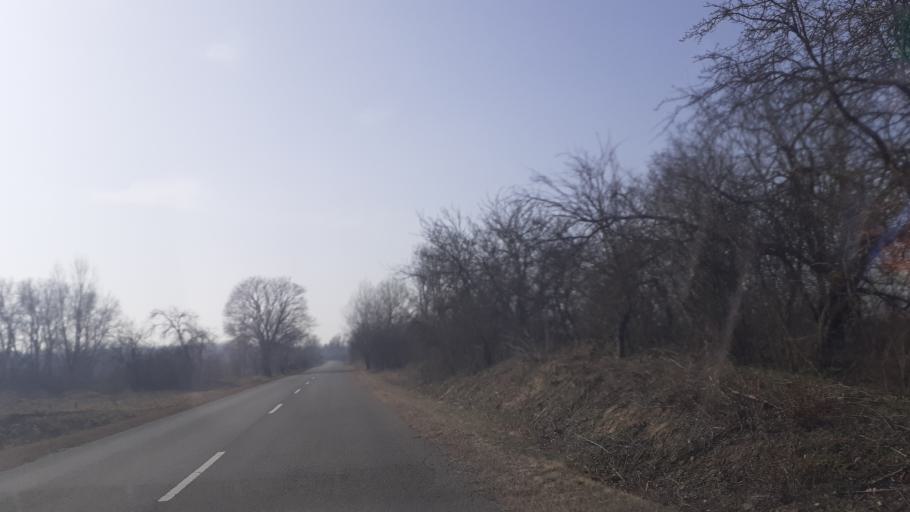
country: HU
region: Pest
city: Orkeny
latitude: 47.1014
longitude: 19.3925
